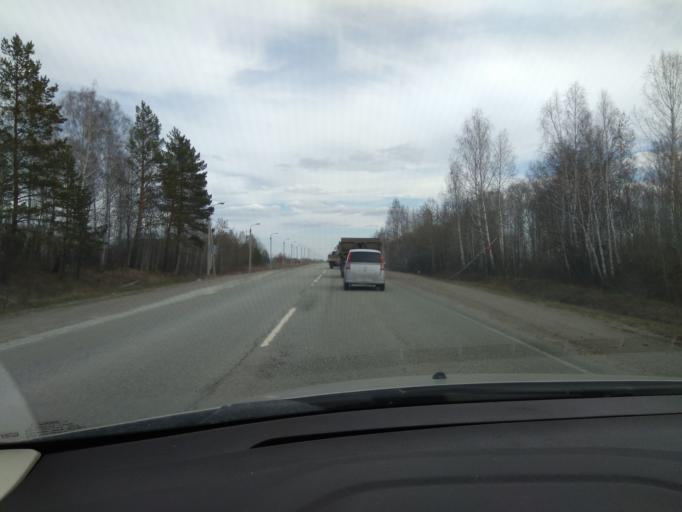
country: RU
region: Sverdlovsk
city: Yelanskiy
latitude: 56.7584
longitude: 62.3375
